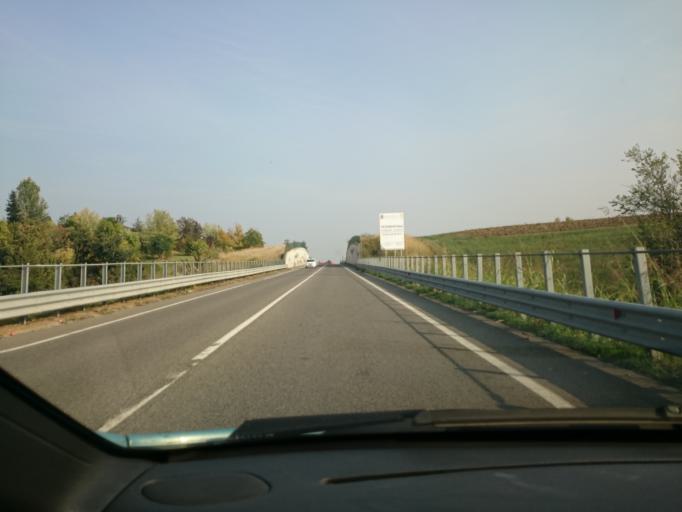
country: IT
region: Emilia-Romagna
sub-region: Provincia di Reggio Emilia
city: Scandiano
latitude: 44.5924
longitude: 10.7114
